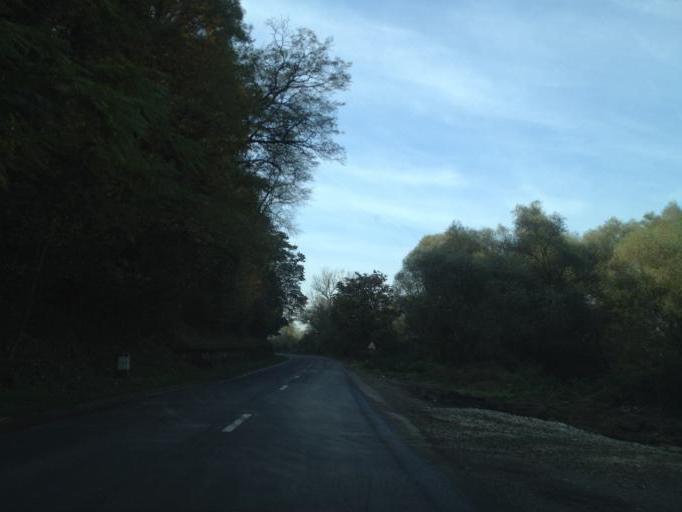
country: RO
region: Hunedoara
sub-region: Comuna Ilia
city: Ilia
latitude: 45.9214
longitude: 22.6673
